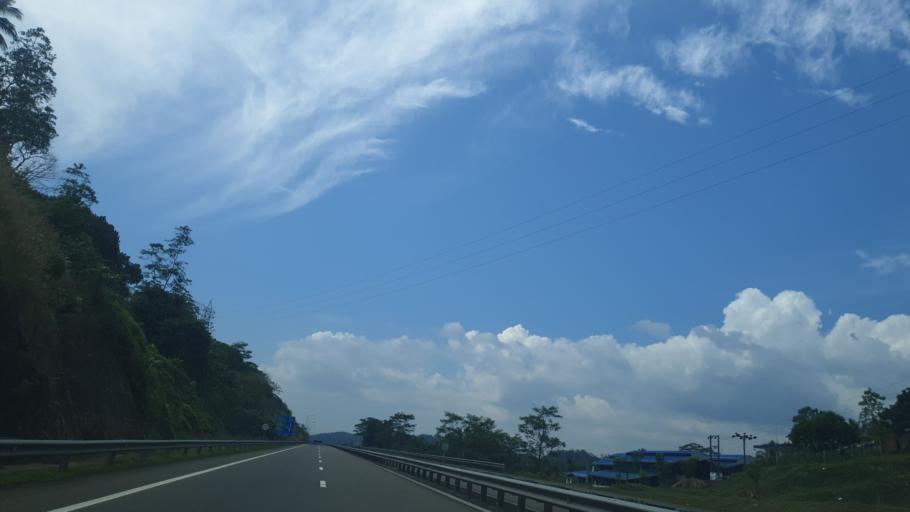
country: LK
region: Southern
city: Weligama
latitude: 6.0329
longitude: 80.3748
